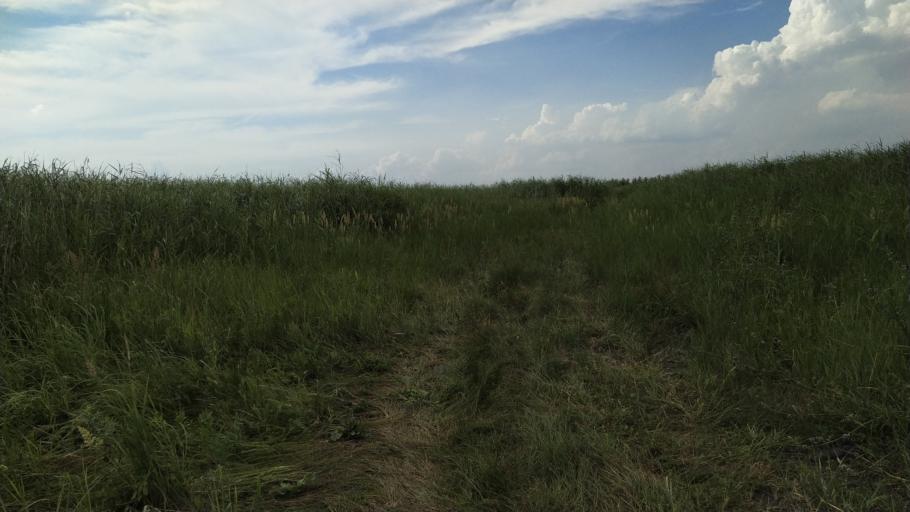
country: RU
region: Rostov
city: Kuleshovka
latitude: 47.1249
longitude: 39.6190
